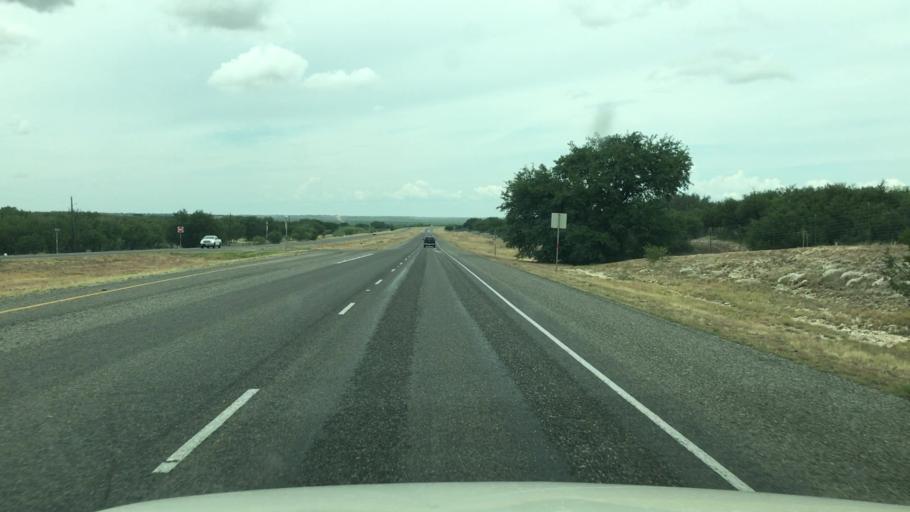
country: US
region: Texas
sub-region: Concho County
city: Eden
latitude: 31.2328
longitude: -99.9914
